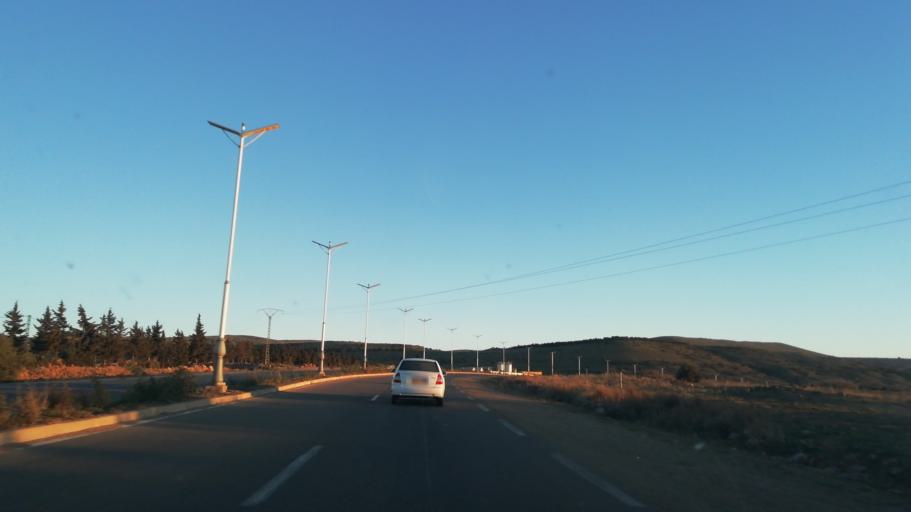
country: DZ
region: Saida
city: Saida
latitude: 34.8590
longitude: 0.1967
